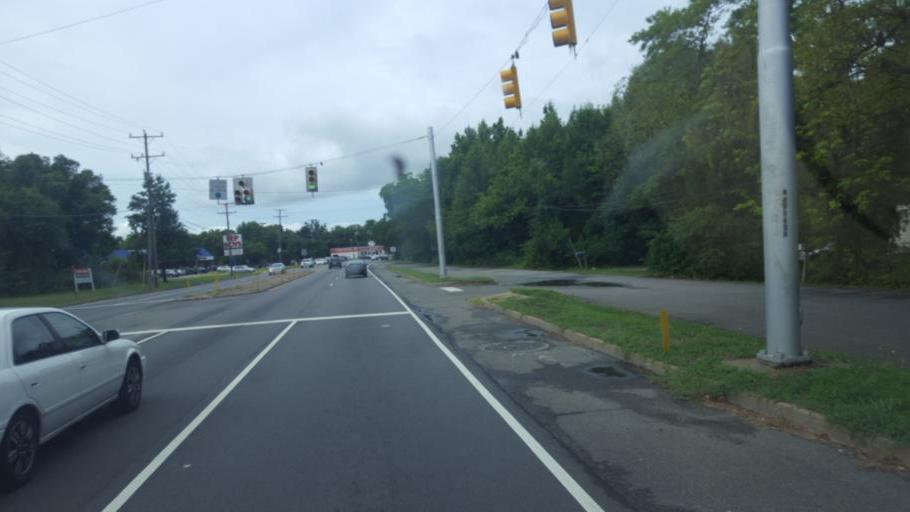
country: US
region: Virginia
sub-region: Henrico County
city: Montrose
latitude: 37.5427
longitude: -77.3720
